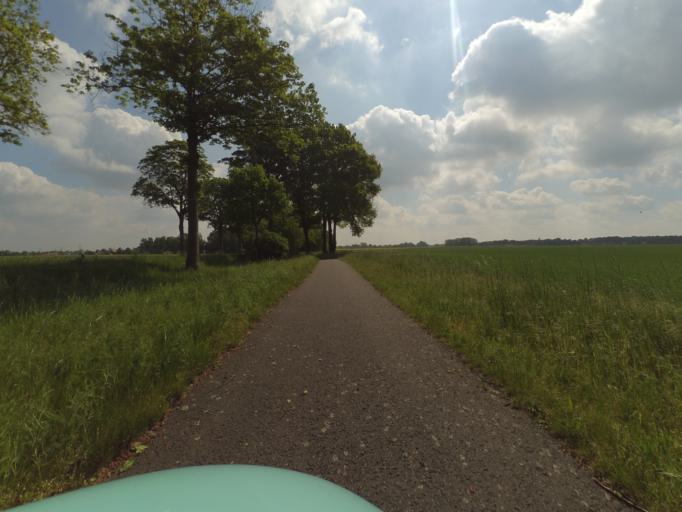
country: DE
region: Lower Saxony
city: Edemissen
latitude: 52.3978
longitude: 10.3128
